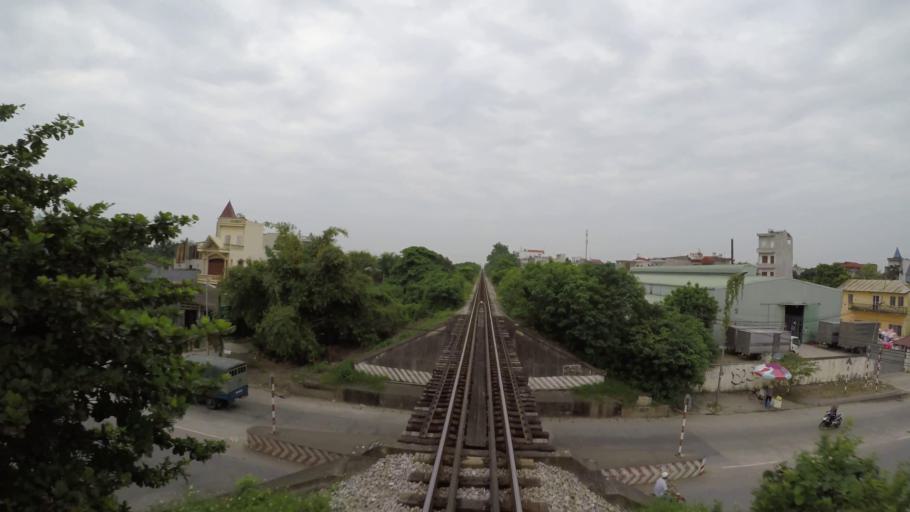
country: VN
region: Hai Duong
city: Thanh Pho Hai Duong
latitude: 20.9496
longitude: 106.3619
